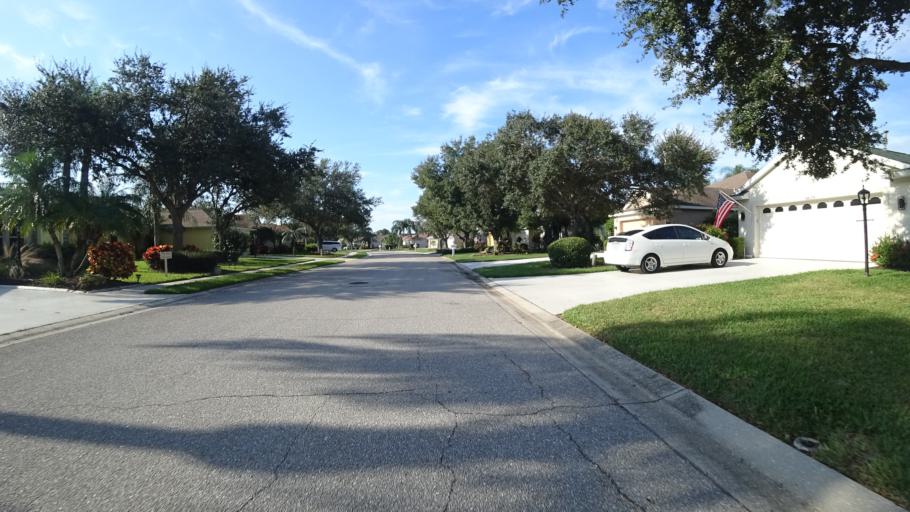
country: US
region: Florida
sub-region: Sarasota County
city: Desoto Lakes
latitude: 27.4228
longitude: -82.4961
